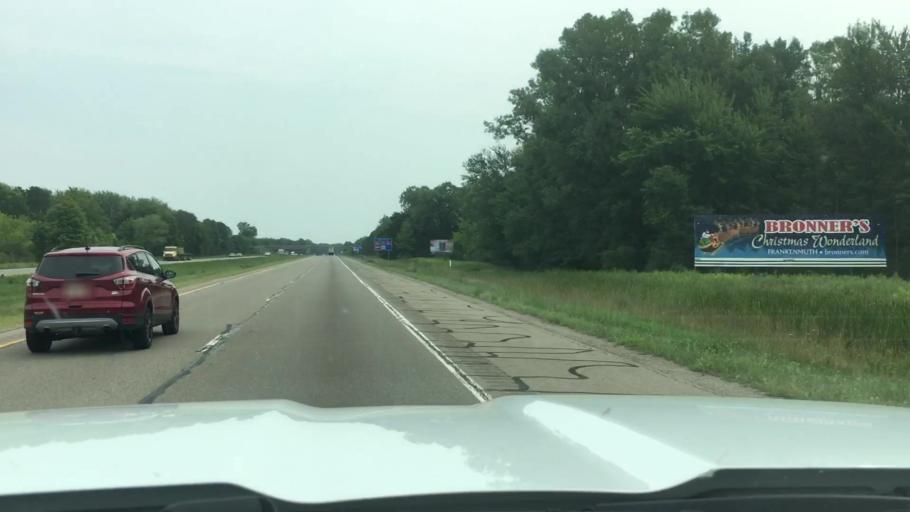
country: US
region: Michigan
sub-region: Eaton County
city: Dimondale
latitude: 42.6654
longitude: -84.6112
